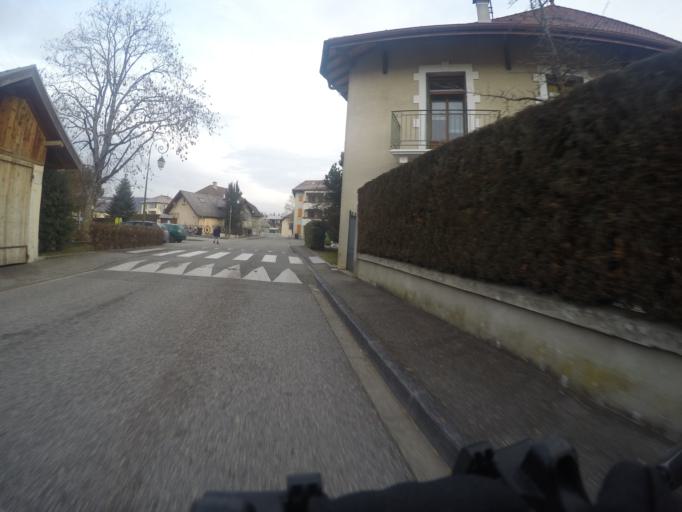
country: FR
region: Rhone-Alpes
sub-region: Departement de la Haute-Savoie
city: Metz-Tessy
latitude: 45.9329
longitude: 6.1101
